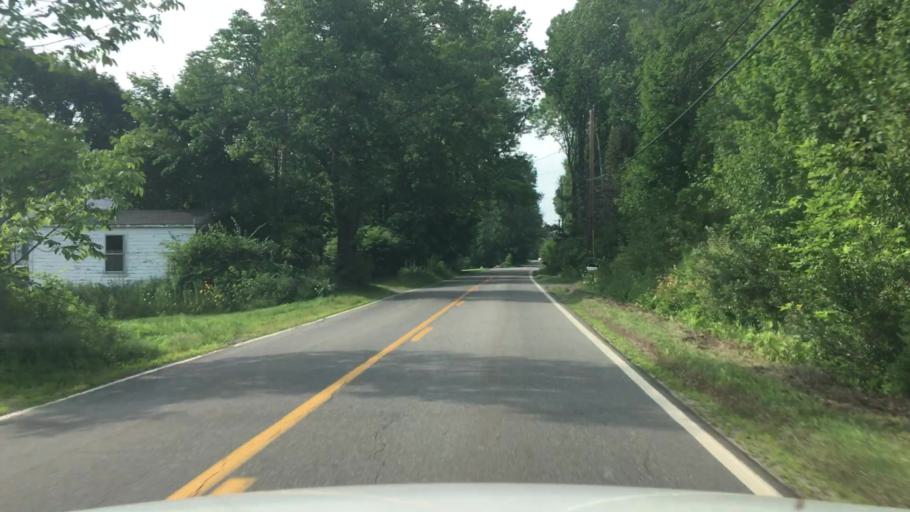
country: US
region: Maine
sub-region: Lincoln County
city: Waldoboro
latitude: 44.1574
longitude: -69.3762
